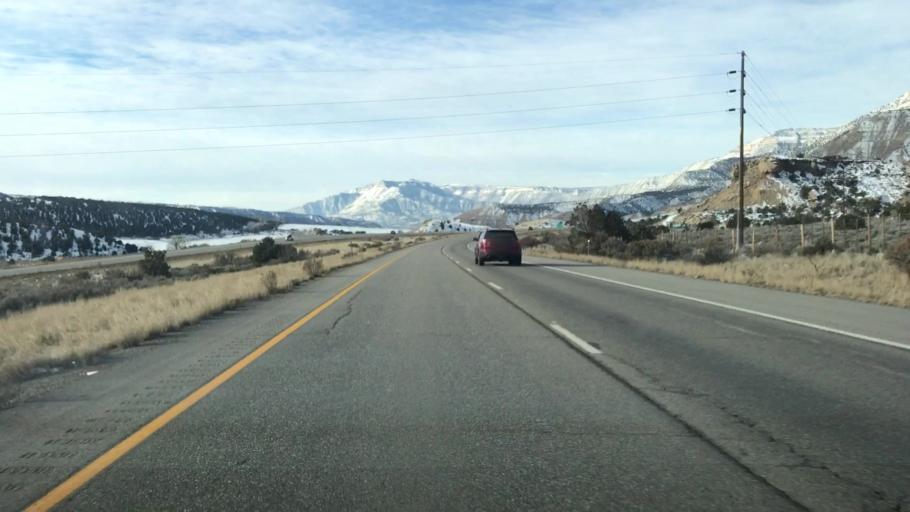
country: US
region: Colorado
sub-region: Garfield County
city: Battlement Mesa
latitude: 39.4999
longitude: -107.9141
